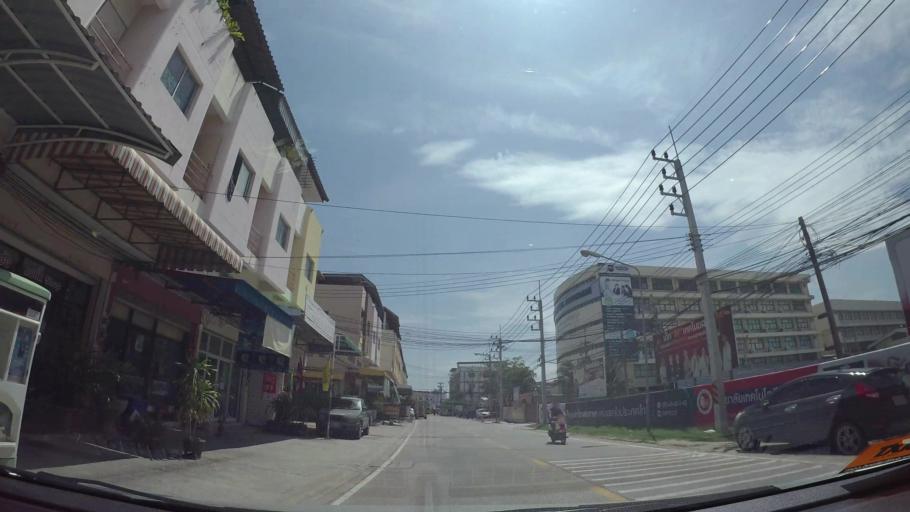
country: TH
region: Chon Buri
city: Chon Buri
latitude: 13.3220
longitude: 100.9562
